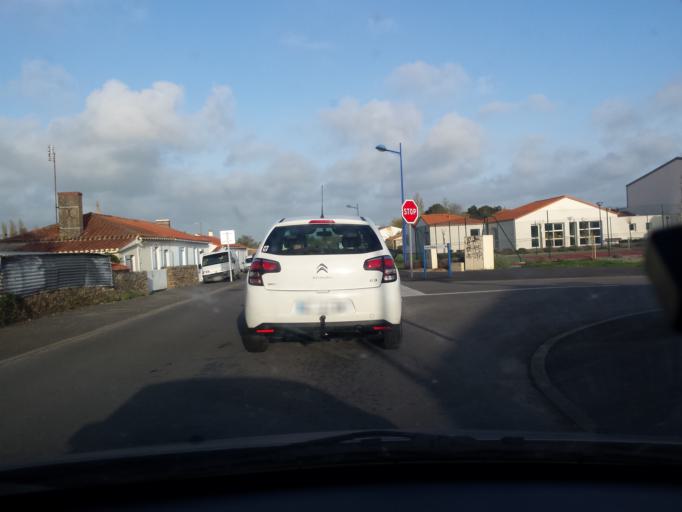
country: FR
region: Pays de la Loire
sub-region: Departement de la Vendee
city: Saint-Mathurin
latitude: 46.5644
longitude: -1.7185
